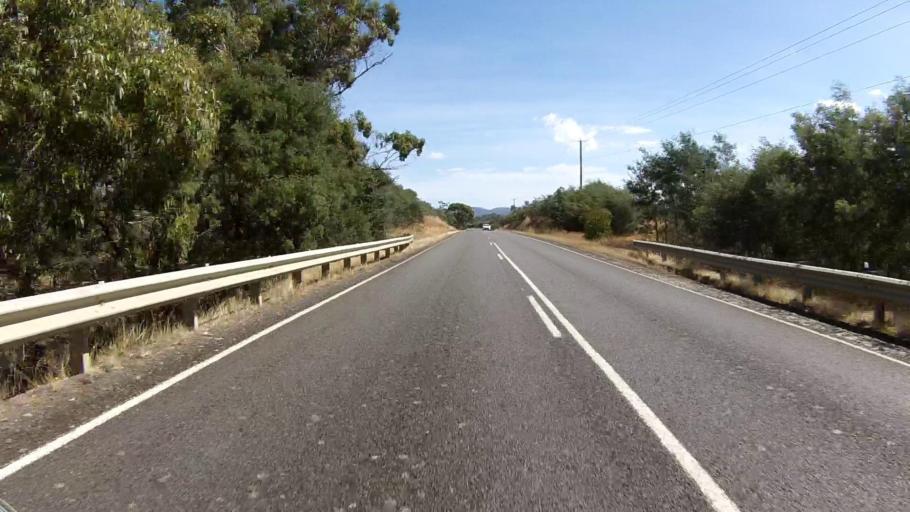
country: AU
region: Tasmania
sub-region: Sorell
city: Sorell
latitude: -42.5928
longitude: 147.7944
